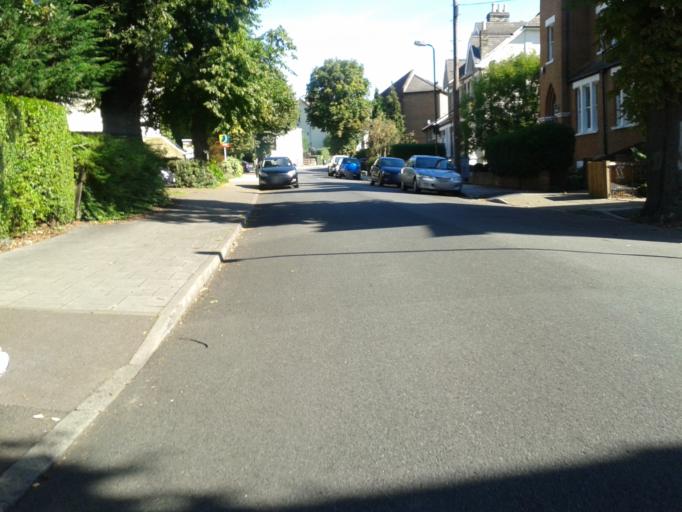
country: GB
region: England
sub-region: Greater London
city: Thornton Heath
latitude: 51.4128
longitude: -0.0737
